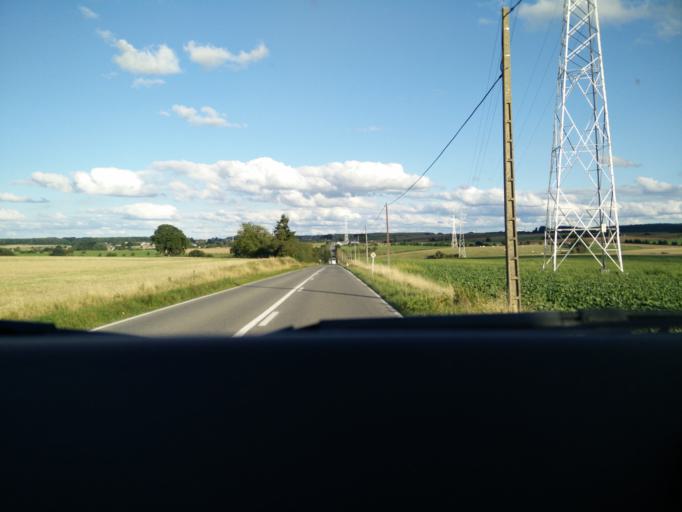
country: BE
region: Wallonia
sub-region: Province de Namur
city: Walcourt
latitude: 50.2208
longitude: 4.4325
